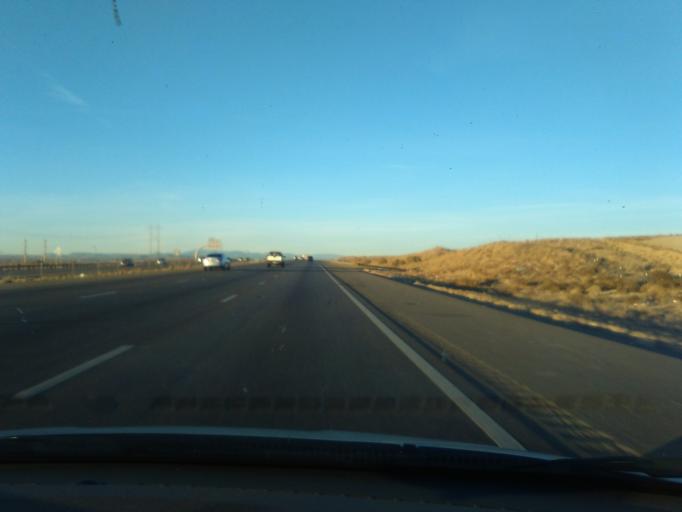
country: US
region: New Mexico
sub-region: Sandoval County
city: Corrales
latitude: 35.2191
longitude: -106.5734
